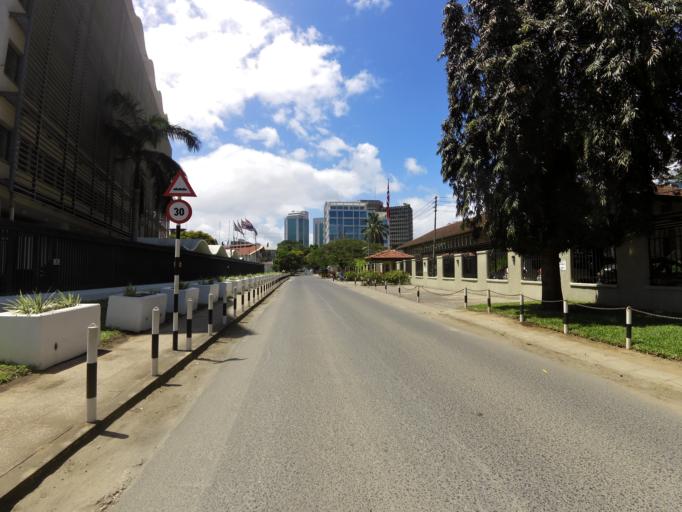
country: TZ
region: Dar es Salaam
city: Dar es Salaam
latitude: -6.8123
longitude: 39.2911
